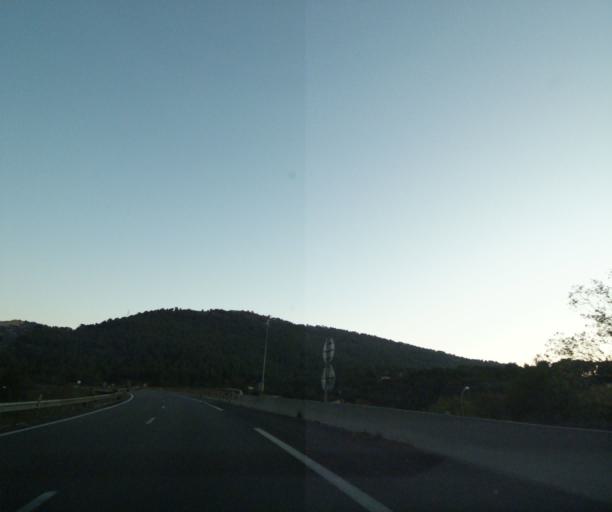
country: FR
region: Provence-Alpes-Cote d'Azur
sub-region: Departement des Bouches-du-Rhone
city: Aubagne
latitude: 43.2809
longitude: 5.5840
